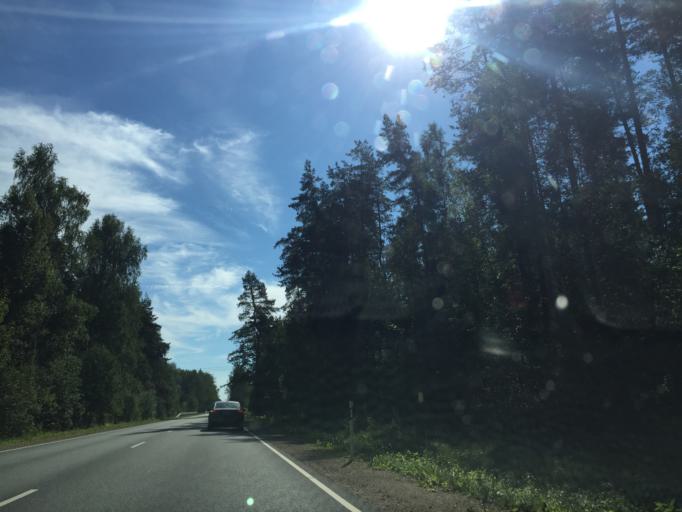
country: LV
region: Ikskile
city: Ikskile
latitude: 56.8894
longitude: 24.4817
